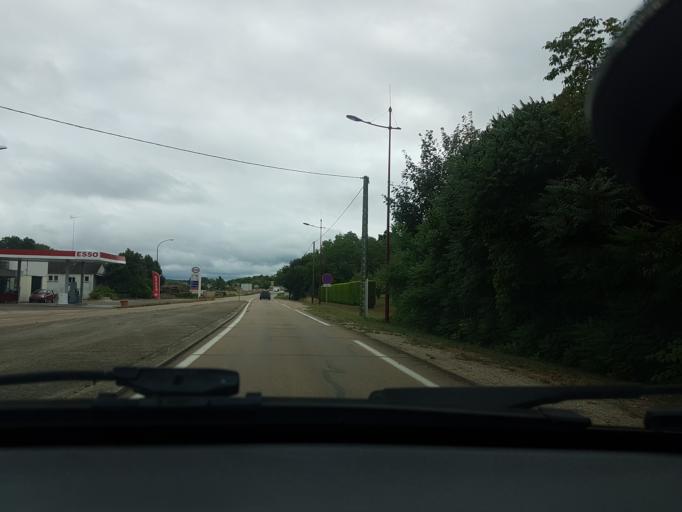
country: FR
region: Bourgogne
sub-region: Departement de l'Yonne
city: Champs-sur-Yonne
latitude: 47.7037
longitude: 3.6272
